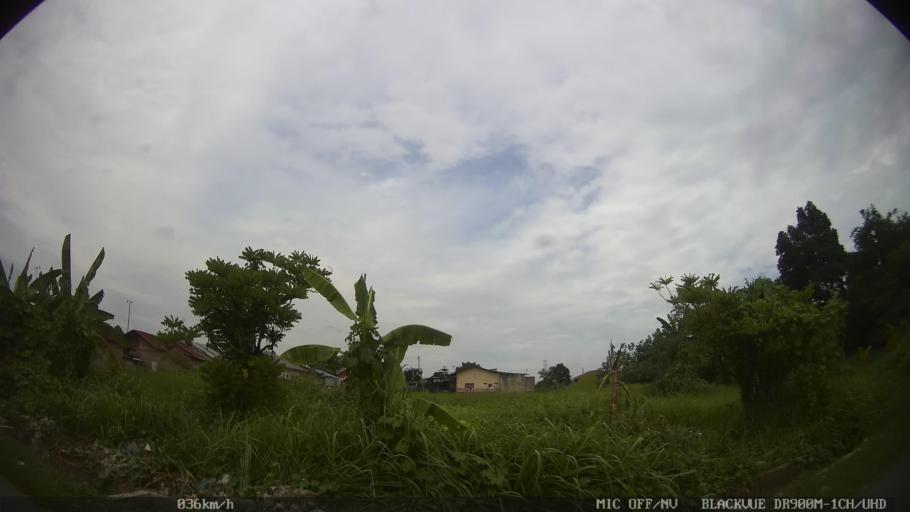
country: ID
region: North Sumatra
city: Sunggal
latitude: 3.6158
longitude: 98.6005
